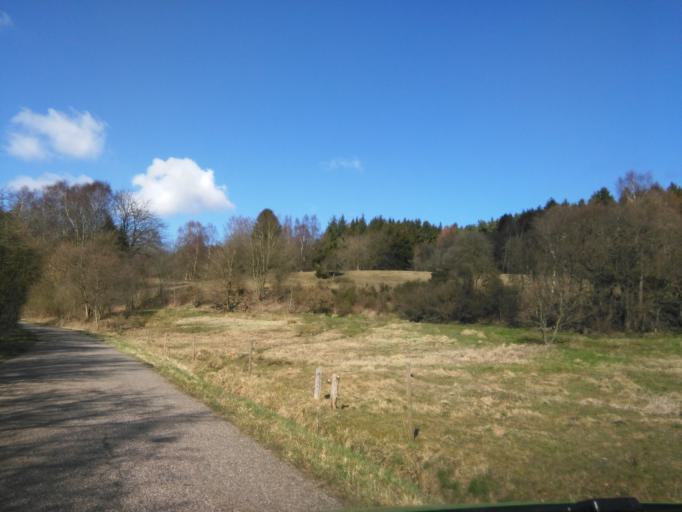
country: DK
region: Central Jutland
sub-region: Skanderborg Kommune
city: Ry
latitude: 56.1026
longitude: 9.7405
